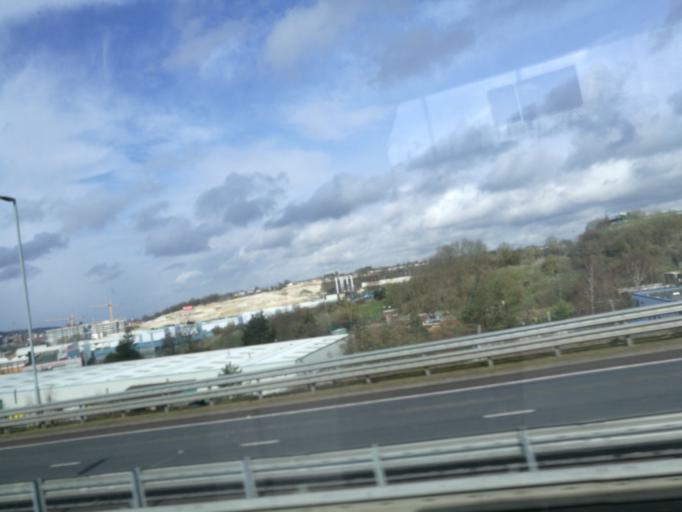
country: GB
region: England
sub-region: Luton
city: Luton
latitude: 51.8734
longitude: -0.3857
